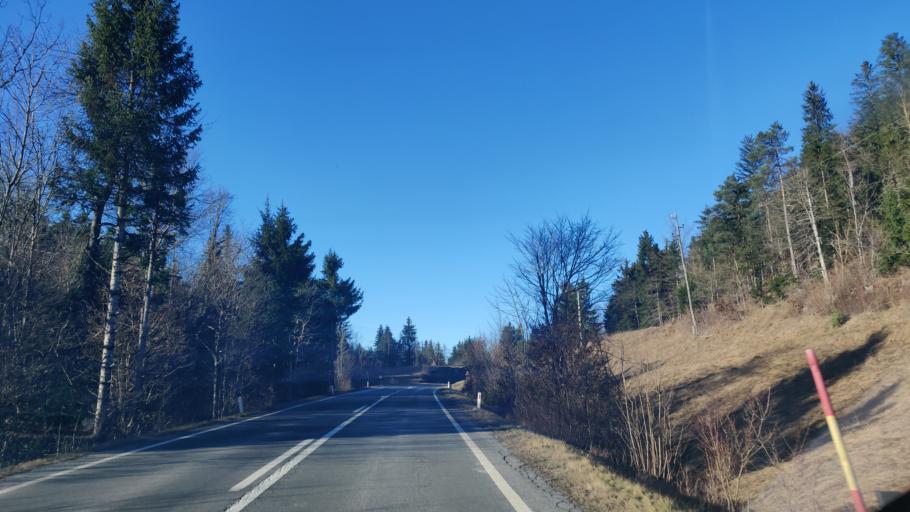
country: SI
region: Logatec
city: Logatec
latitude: 45.8810
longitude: 14.2058
